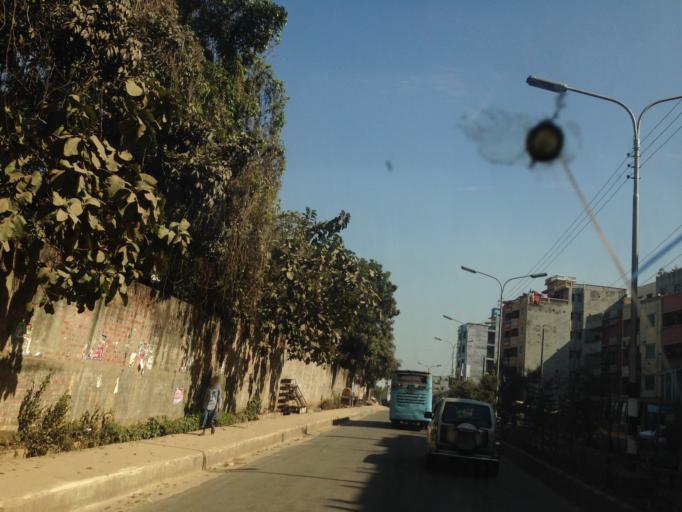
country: BD
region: Dhaka
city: Tungi
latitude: 23.8294
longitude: 90.3703
